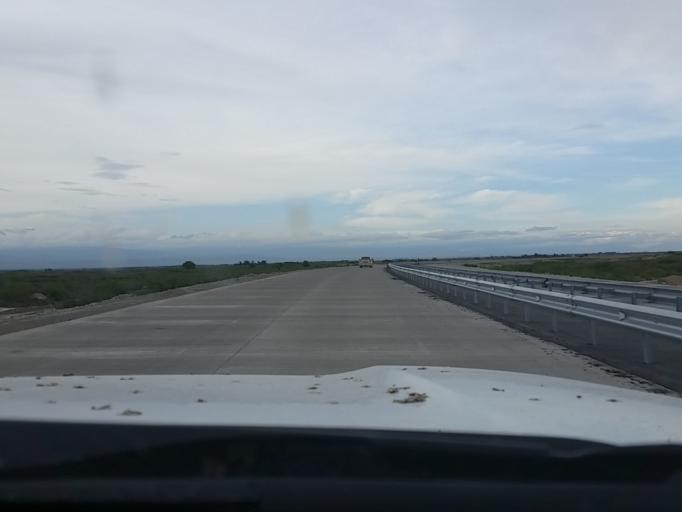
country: KZ
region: Almaty Oblysy
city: Zharkent
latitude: 44.0961
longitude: 80.0600
